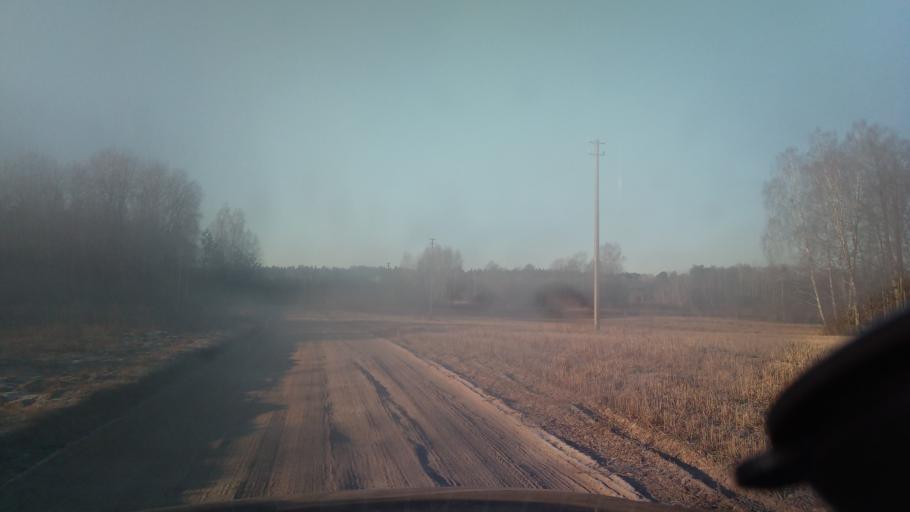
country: LT
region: Alytaus apskritis
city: Druskininkai
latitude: 54.1611
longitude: 23.9587
